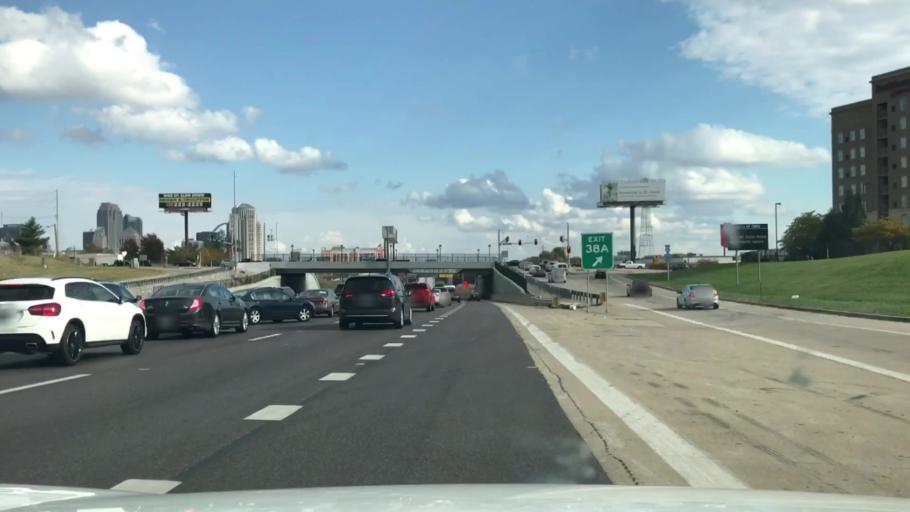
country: US
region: Missouri
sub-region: City of Saint Louis
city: St. Louis
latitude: 38.6280
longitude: -90.2198
